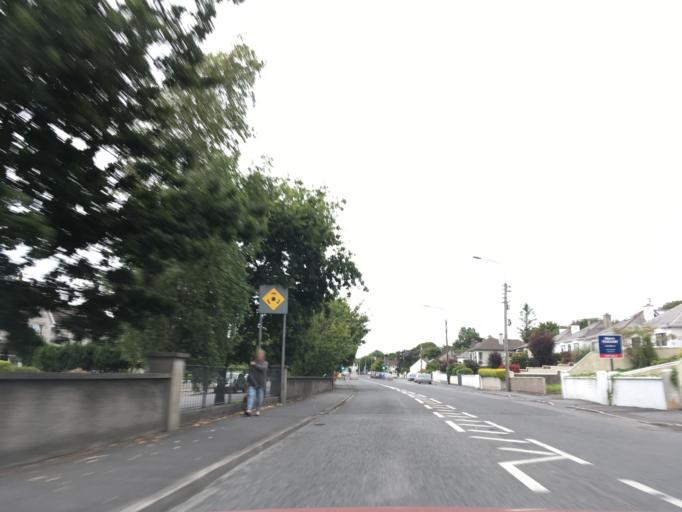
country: IE
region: Munster
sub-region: An Clar
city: Ennis
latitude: 52.8447
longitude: -8.9748
